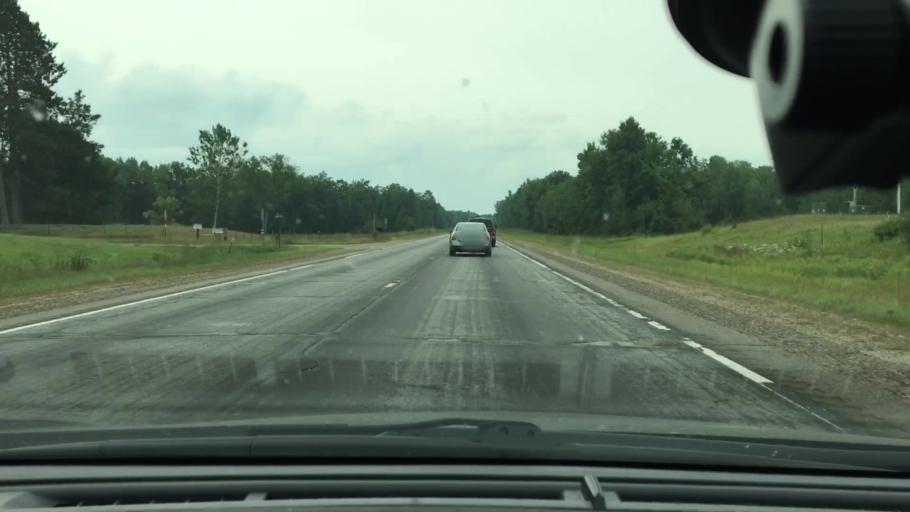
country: US
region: Minnesota
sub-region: Crow Wing County
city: Cross Lake
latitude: 46.6792
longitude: -93.9529
